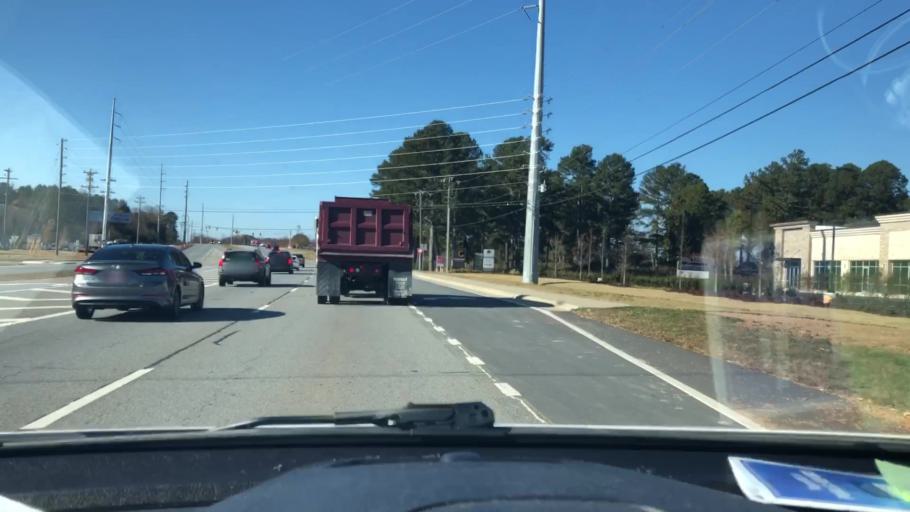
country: US
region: Georgia
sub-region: Fulton County
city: Johns Creek
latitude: 34.0918
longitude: -84.1698
